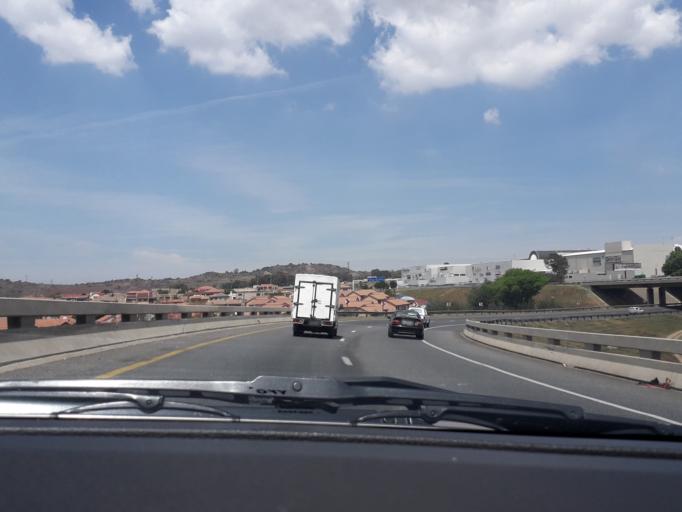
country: ZA
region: Gauteng
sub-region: City of Johannesburg Metropolitan Municipality
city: Johannesburg
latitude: -26.2626
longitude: 27.9865
